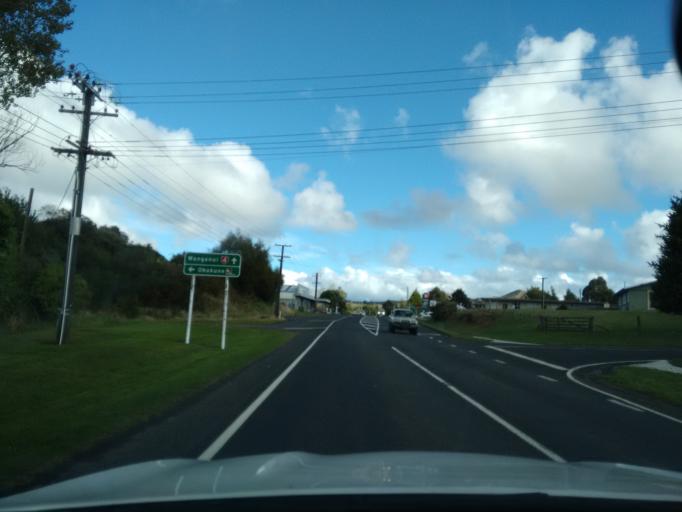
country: NZ
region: Manawatu-Wanganui
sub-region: Ruapehu District
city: Waiouru
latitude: -39.4262
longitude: 175.2818
